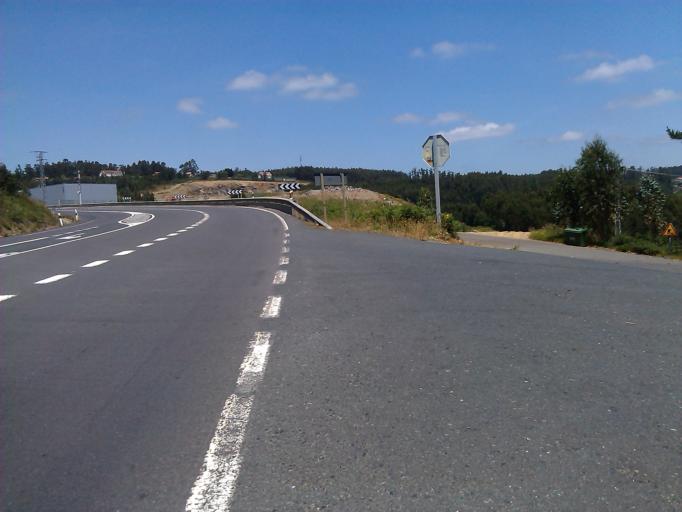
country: ES
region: Galicia
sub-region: Provincia da Coruna
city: Oroso
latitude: 42.9111
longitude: -8.4063
